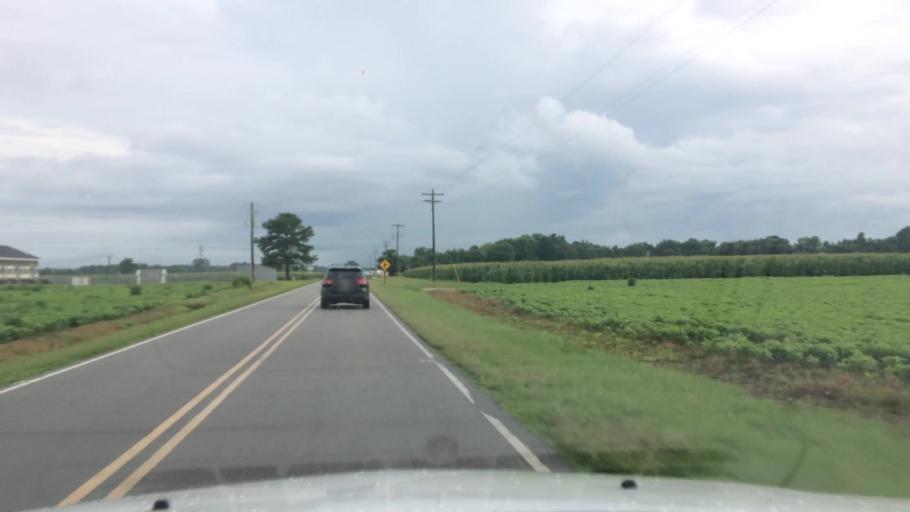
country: US
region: North Carolina
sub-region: Pitt County
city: Farmville
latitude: 35.5774
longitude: -77.5512
